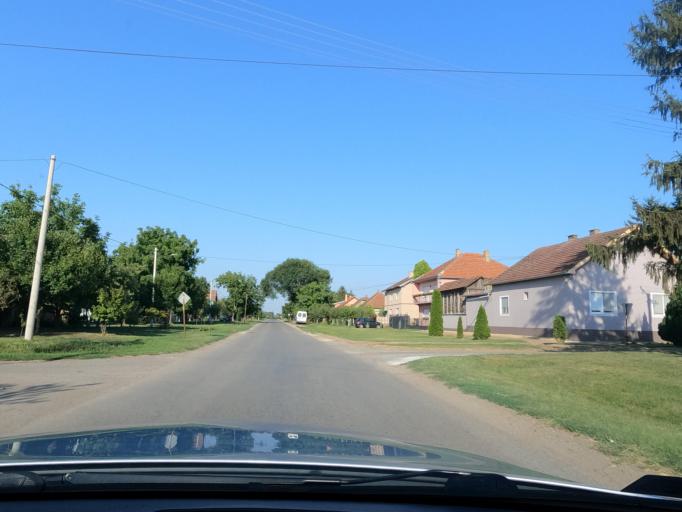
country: RS
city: Curug
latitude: 45.4615
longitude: 20.0632
